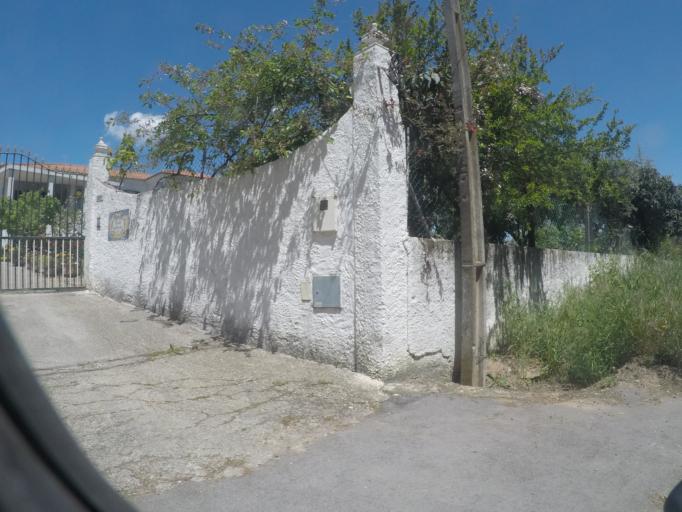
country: PT
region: Setubal
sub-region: Sesimbra
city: Sesimbra
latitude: 38.4600
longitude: -9.0686
